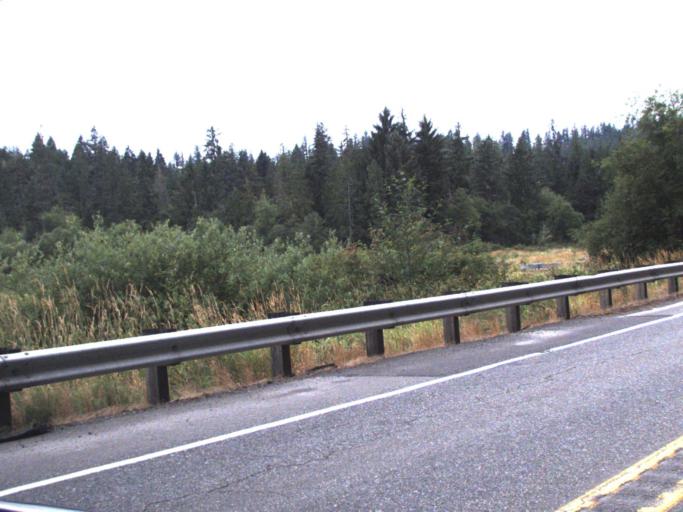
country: US
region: Washington
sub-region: King County
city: Ames Lake
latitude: 47.5917
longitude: -121.9576
